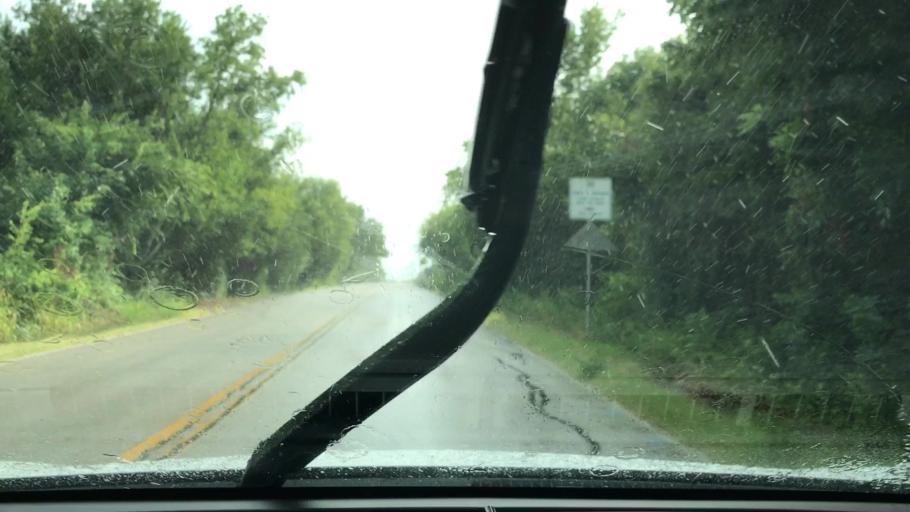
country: US
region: Texas
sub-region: Rockwall County
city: Rockwall
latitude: 32.9507
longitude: -96.5209
